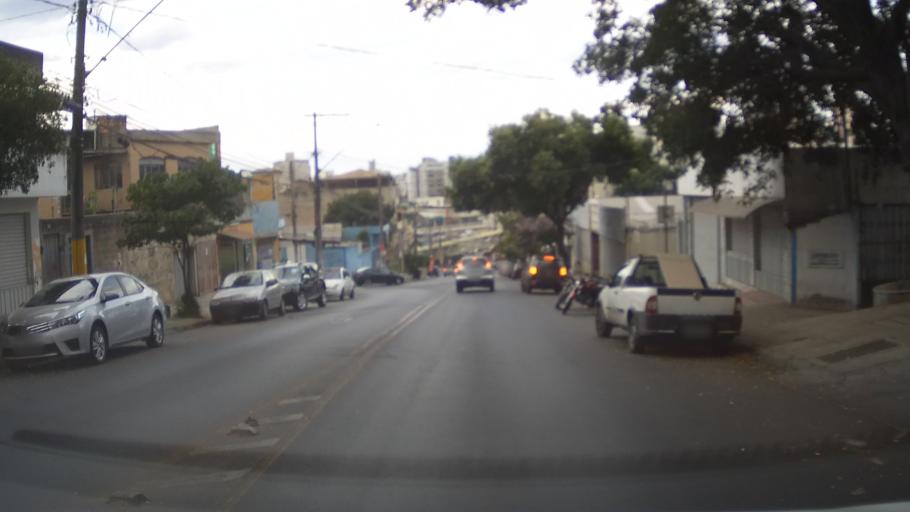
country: BR
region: Minas Gerais
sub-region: Belo Horizonte
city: Belo Horizonte
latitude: -19.8873
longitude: -43.9304
